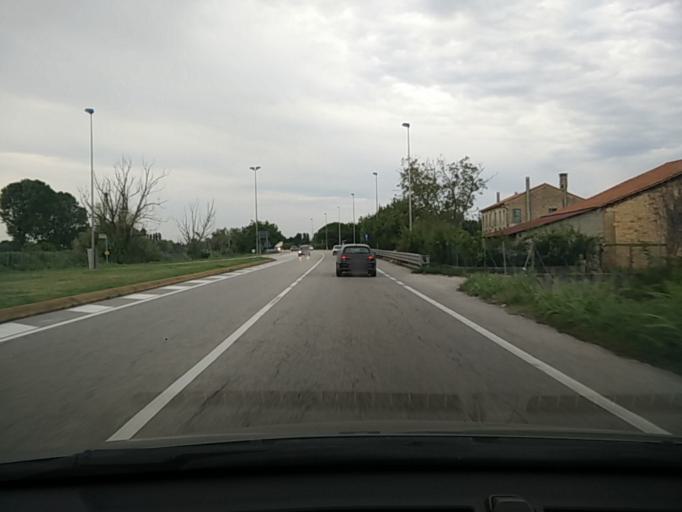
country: IT
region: Veneto
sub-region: Provincia di Venezia
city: Passarella
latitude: 45.5605
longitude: 12.5741
